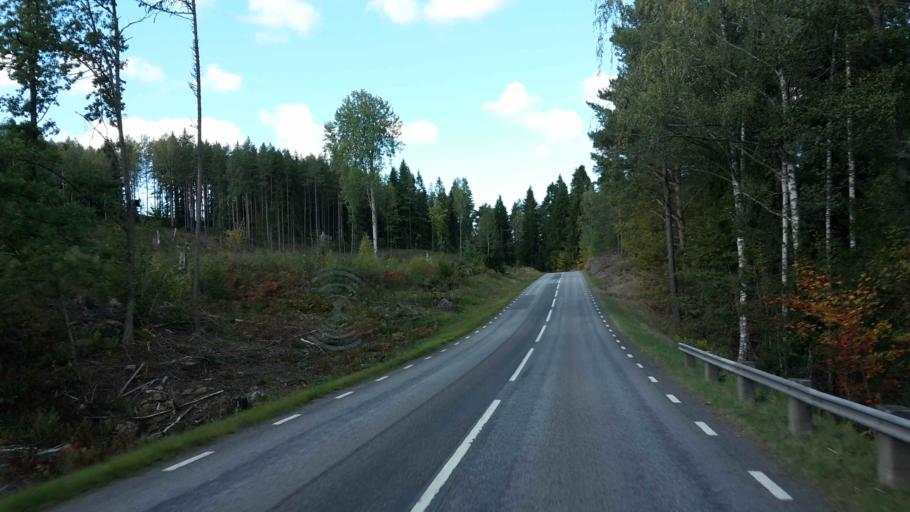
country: SE
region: OEstergoetland
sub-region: Atvidabergs Kommun
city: Atvidaberg
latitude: 58.1722
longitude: 16.1345
